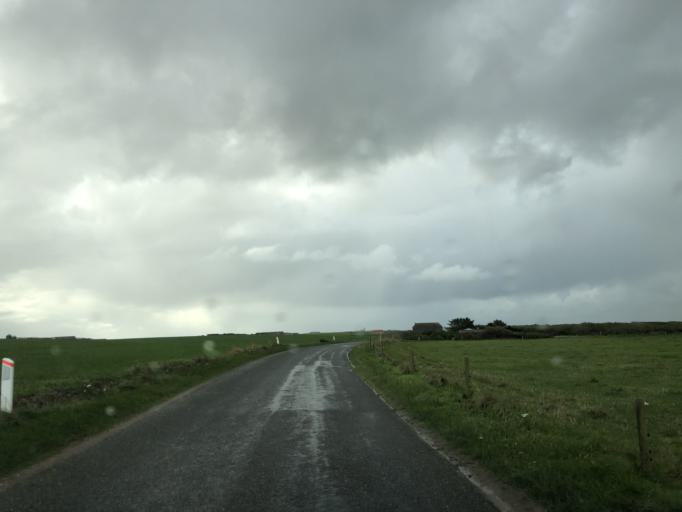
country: DK
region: Central Jutland
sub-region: Lemvig Kommune
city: Harboore
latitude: 56.5447
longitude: 8.1383
